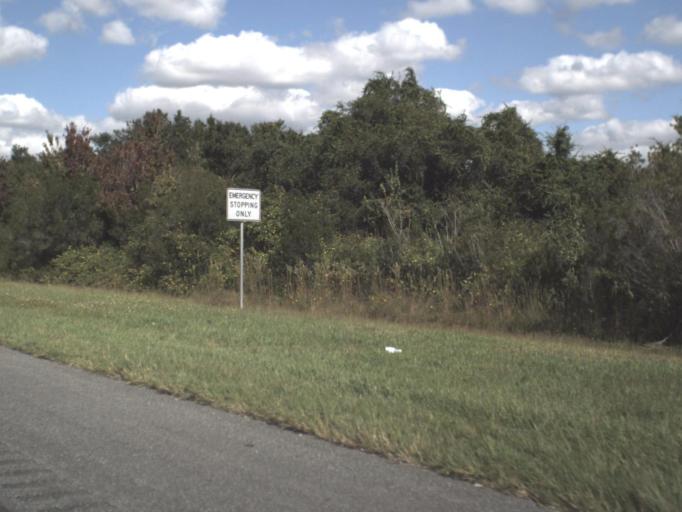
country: US
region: Florida
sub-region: Osceola County
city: Buenaventura Lakes
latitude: 28.2968
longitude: -81.3555
